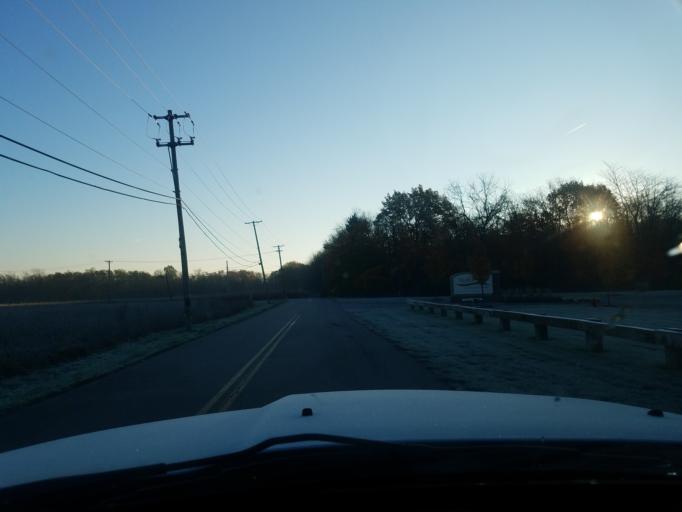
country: US
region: Indiana
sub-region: Montgomery County
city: Crawfordsville
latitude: 40.0685
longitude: -86.9033
